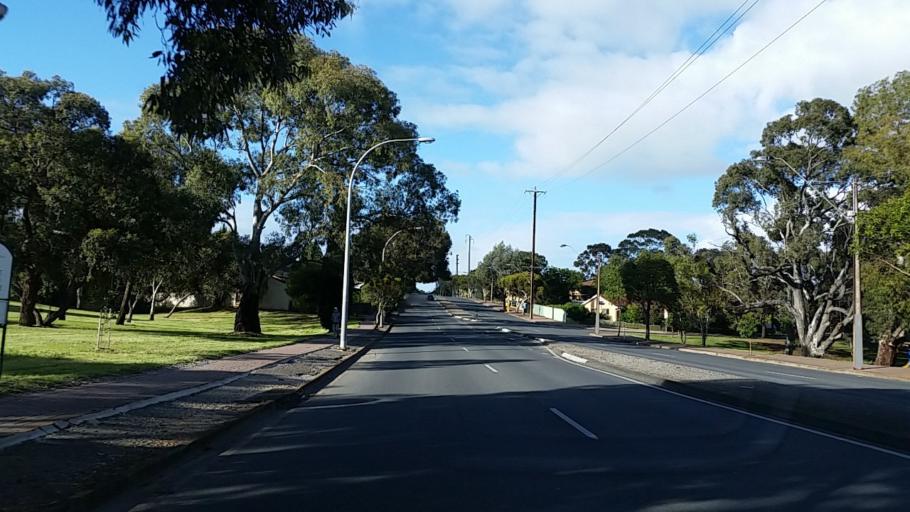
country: AU
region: South Australia
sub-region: Mitcham
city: Clapham
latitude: -35.0027
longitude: 138.5899
